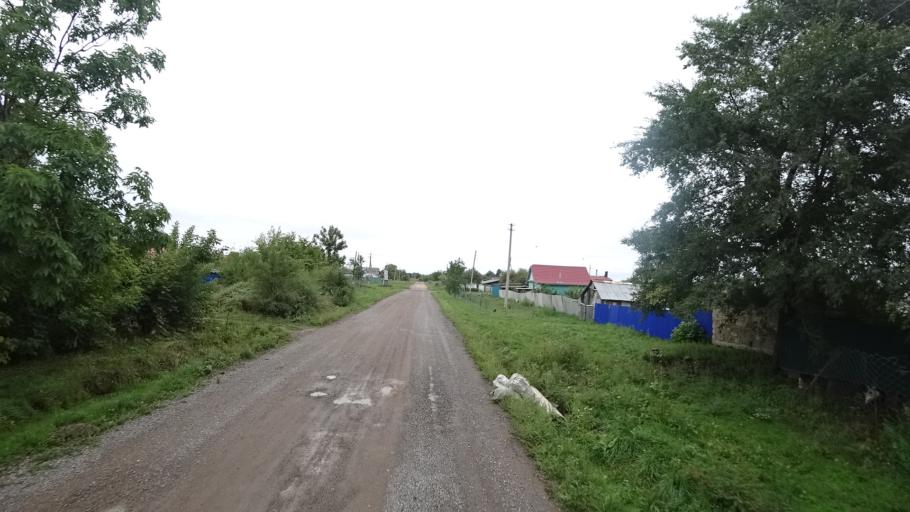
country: RU
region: Primorskiy
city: Chernigovka
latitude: 44.3393
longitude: 132.5620
